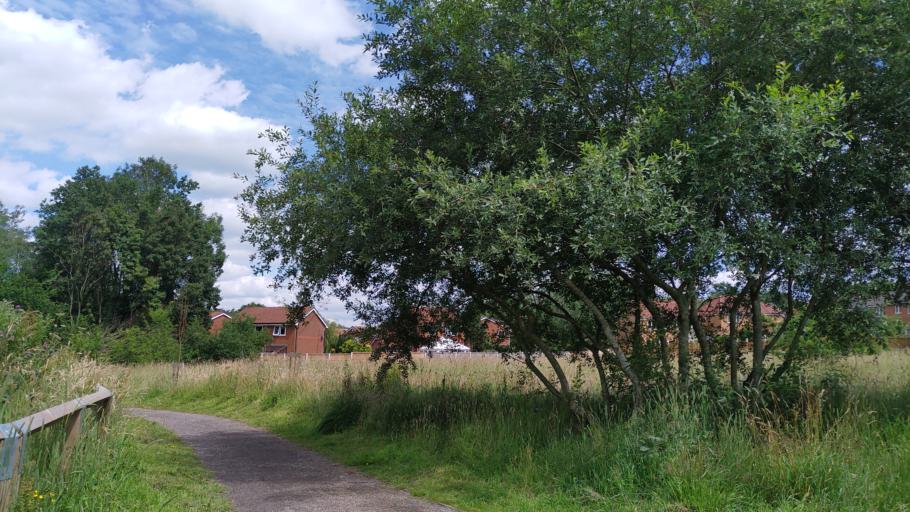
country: GB
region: England
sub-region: Lancashire
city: Coppull
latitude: 53.6343
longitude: -2.6401
